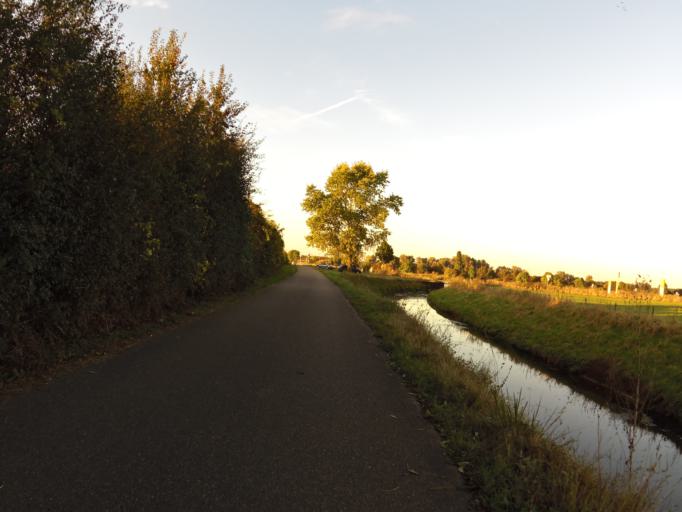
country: NL
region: North Brabant
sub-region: Gemeente Boxmeer
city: Boxmeer
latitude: 51.6411
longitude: 5.9749
